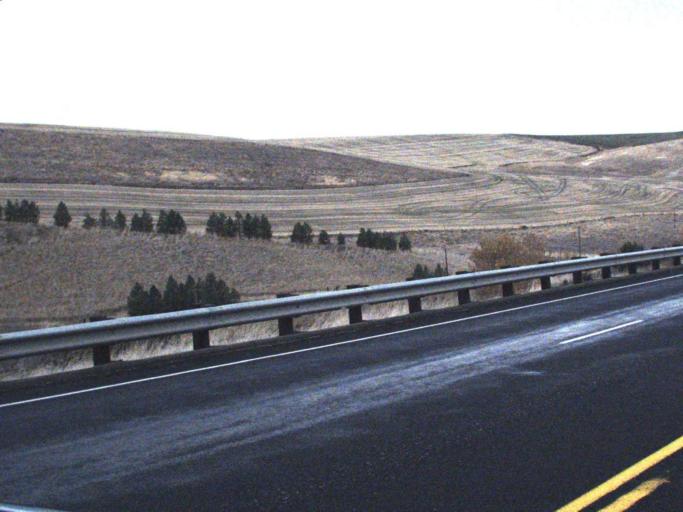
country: US
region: Washington
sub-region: Columbia County
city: Dayton
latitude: 46.4175
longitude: -117.9456
